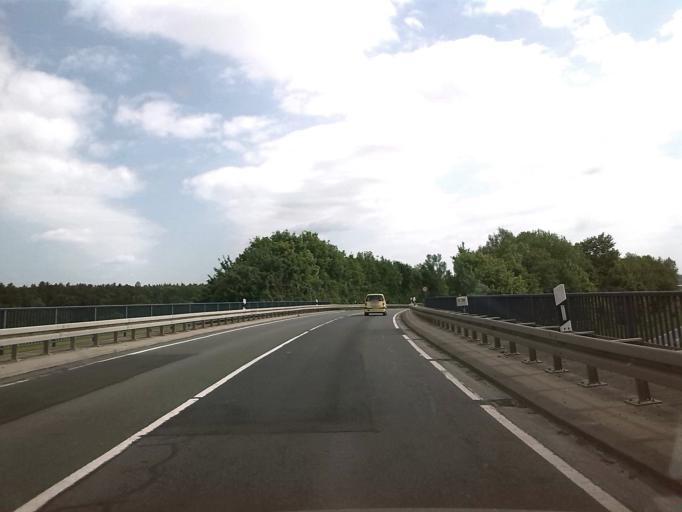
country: DE
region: Hesse
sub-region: Regierungsbezirk Darmstadt
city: Rossdorf
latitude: 49.8752
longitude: 8.7959
